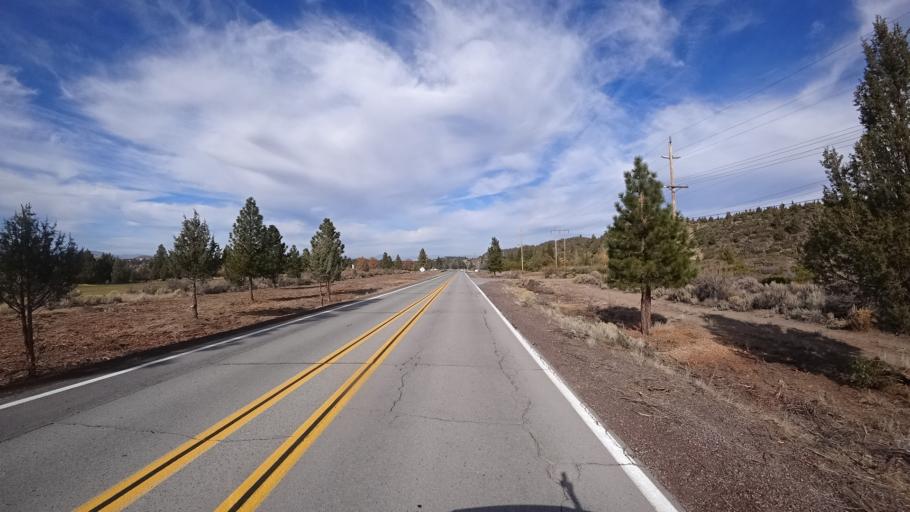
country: US
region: California
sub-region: Siskiyou County
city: Weed
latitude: 41.5060
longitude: -122.3638
